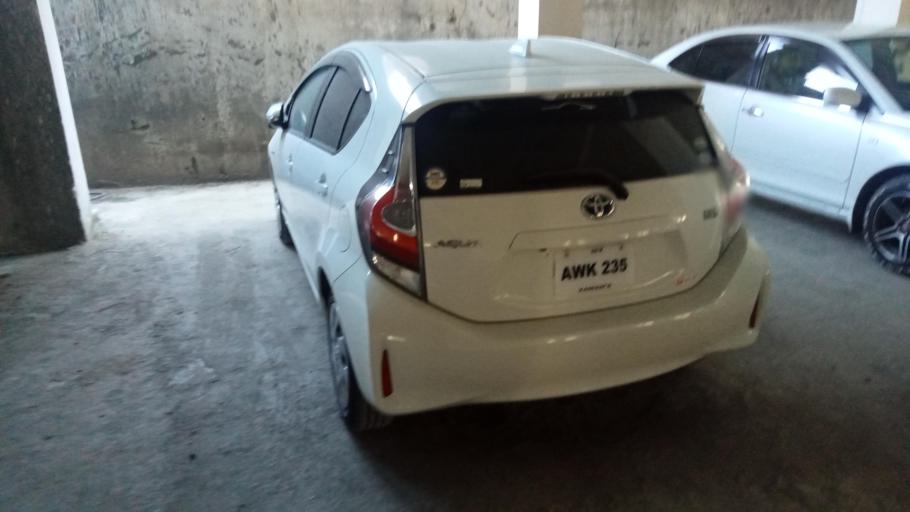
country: PK
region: Khyber Pakhtunkhwa
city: Mingora
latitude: 34.7699
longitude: 72.3595
